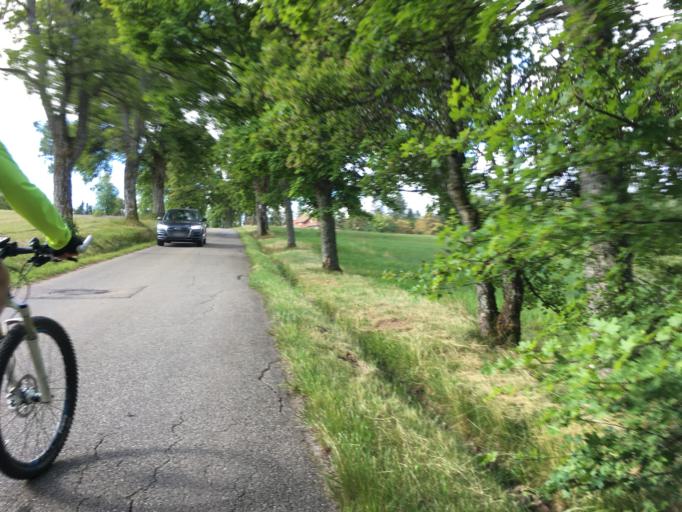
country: DE
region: Baden-Wuerttemberg
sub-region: Karlsruhe Region
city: Freudenstadt
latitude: 48.4553
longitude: 8.4094
